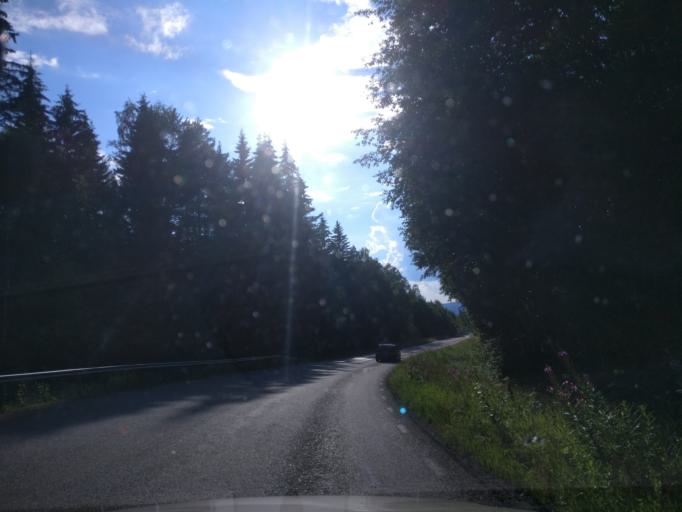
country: SE
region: Dalarna
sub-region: Ludvika Kommun
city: Ludvika
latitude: 60.2640
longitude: 15.0536
